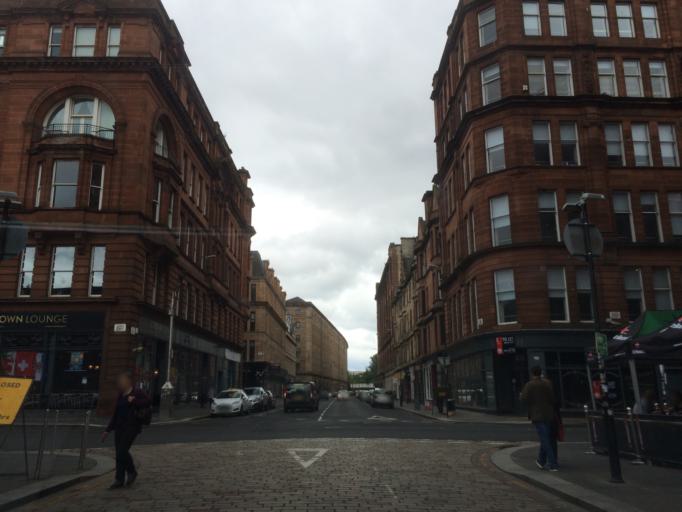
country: GB
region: Scotland
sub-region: Glasgow City
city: Glasgow
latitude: 55.8580
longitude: -4.2449
